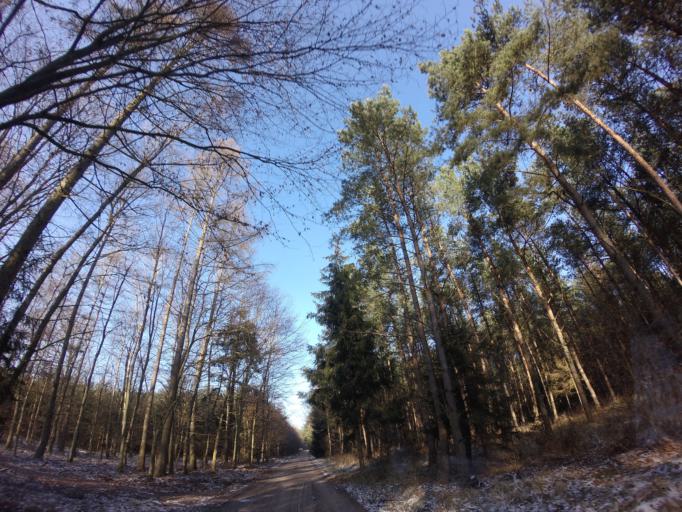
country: PL
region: West Pomeranian Voivodeship
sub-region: Powiat choszczenski
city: Pelczyce
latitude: 52.9527
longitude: 15.3350
